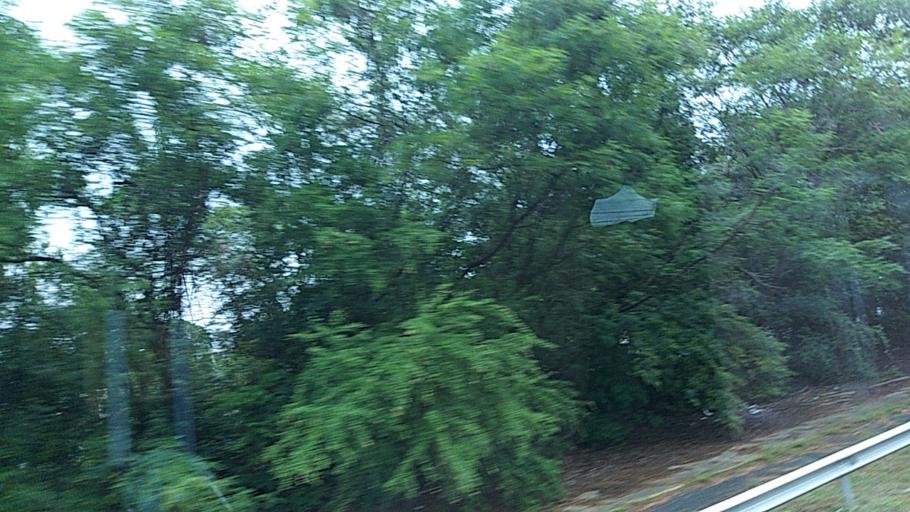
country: TH
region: Nakhon Ratchasima
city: Nakhon Ratchasima
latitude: 15.0560
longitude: 102.1604
